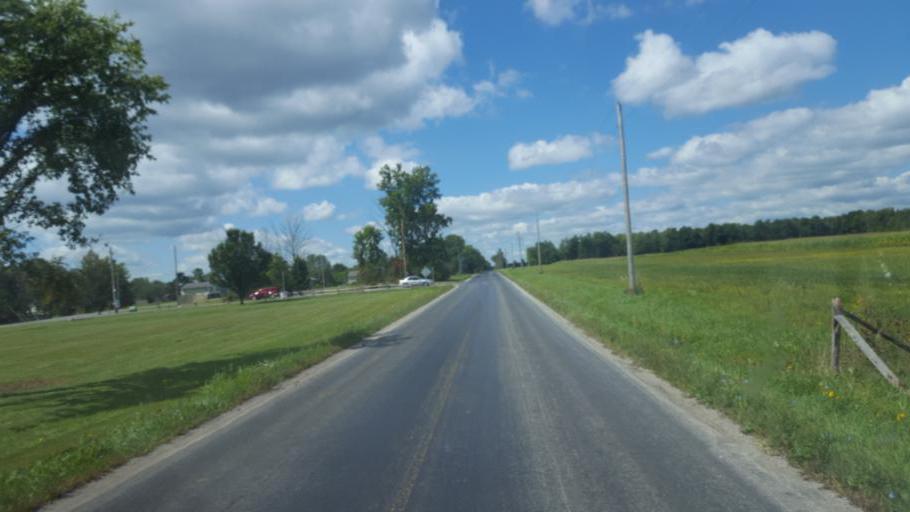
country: US
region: Ohio
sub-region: Wayne County
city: West Salem
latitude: 40.9920
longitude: -82.1855
